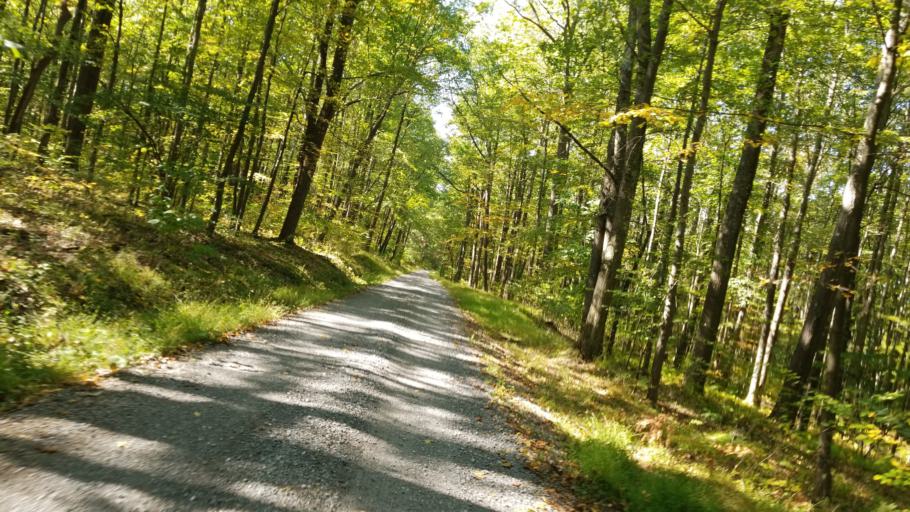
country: US
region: Pennsylvania
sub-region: Clearfield County
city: Clearfield
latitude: 41.1790
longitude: -78.4934
